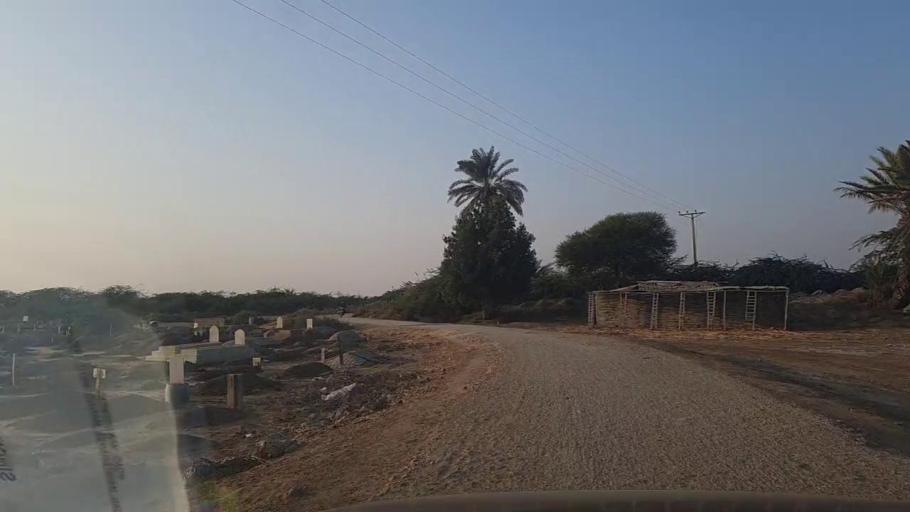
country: PK
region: Sindh
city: Keti Bandar
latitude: 24.3082
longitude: 67.6026
